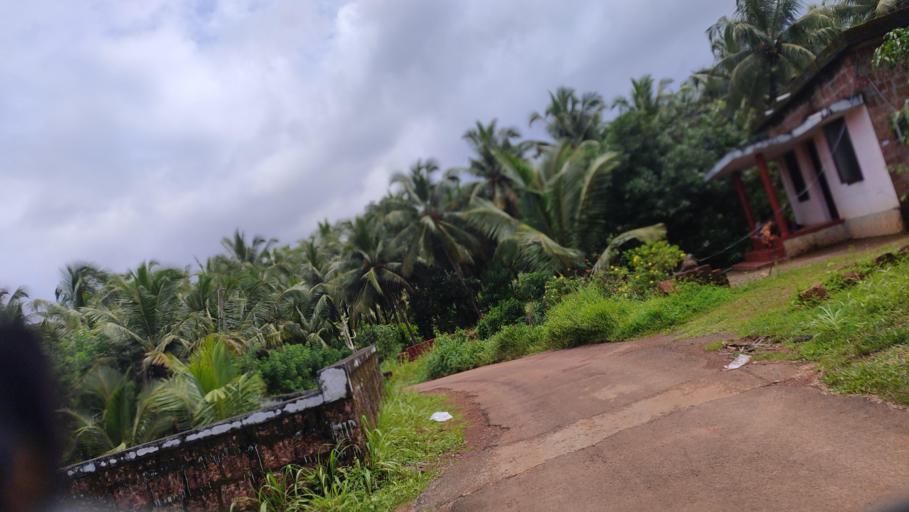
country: IN
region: Kerala
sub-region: Kasaragod District
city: Kannangad
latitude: 12.4001
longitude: 75.0553
